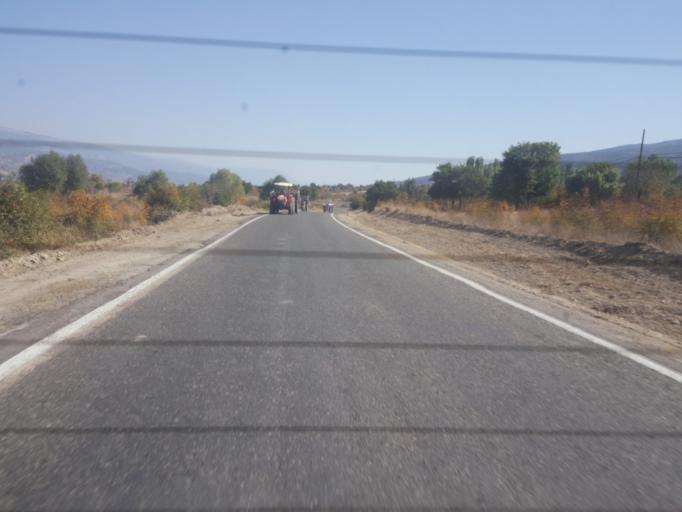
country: TR
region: Kastamonu
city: Tosya
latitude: 40.9988
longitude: 34.1442
